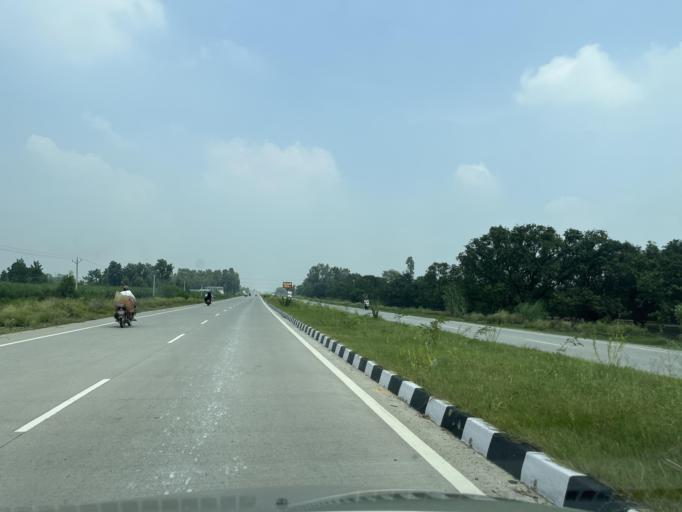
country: IN
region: Uttar Pradesh
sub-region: Bijnor
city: Najibabad
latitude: 29.5511
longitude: 78.3392
